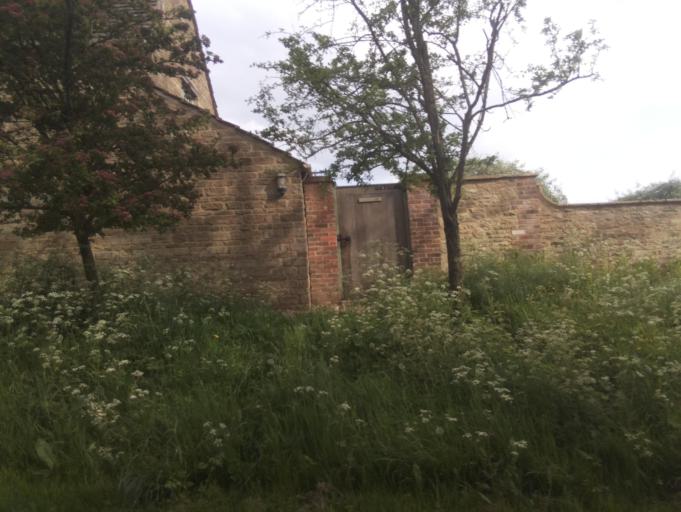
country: GB
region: England
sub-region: Wiltshire
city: Malmesbury
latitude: 51.5482
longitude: -2.0990
